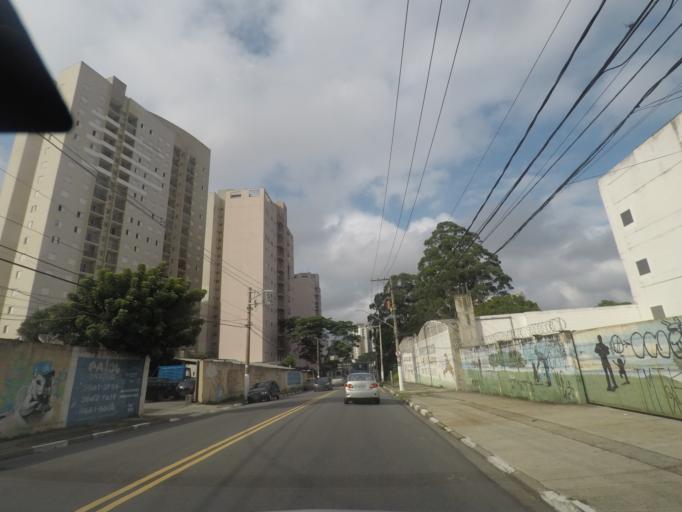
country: BR
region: Sao Paulo
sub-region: Osasco
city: Osasco
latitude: -23.5539
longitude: -46.7784
